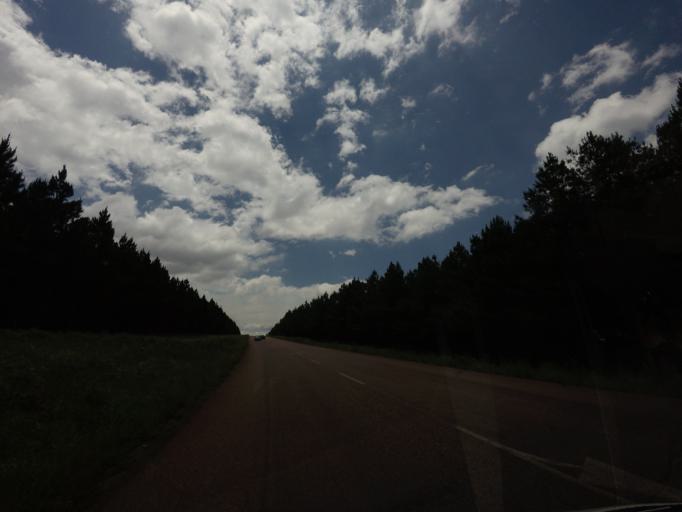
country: ZA
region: Mpumalanga
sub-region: Ehlanzeni District
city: Graksop
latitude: -25.0381
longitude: 30.8204
